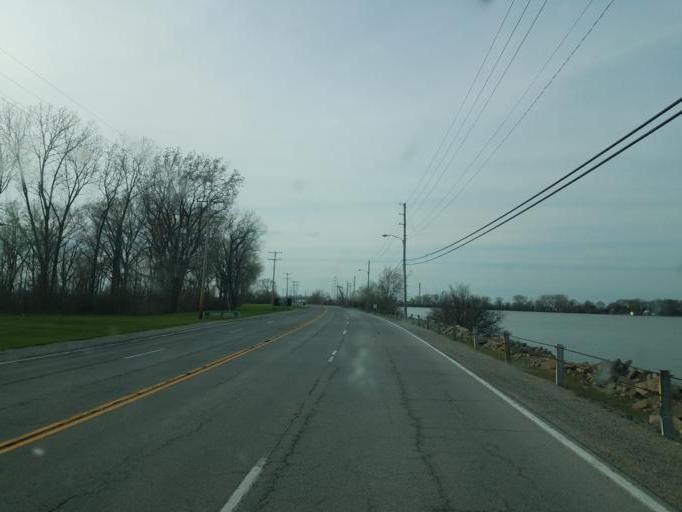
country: US
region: Ohio
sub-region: Erie County
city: Sandusky
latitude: 41.4643
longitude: -82.6722
